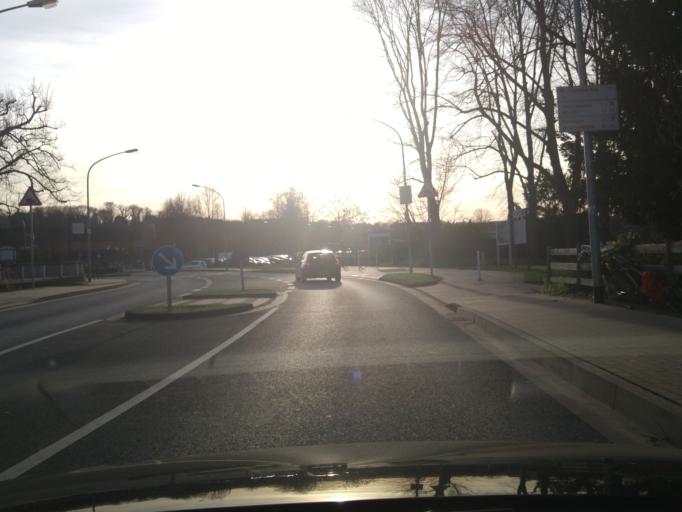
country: DE
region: North Rhine-Westphalia
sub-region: Regierungsbezirk Dusseldorf
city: Velbert
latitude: 51.3938
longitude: 7.0786
